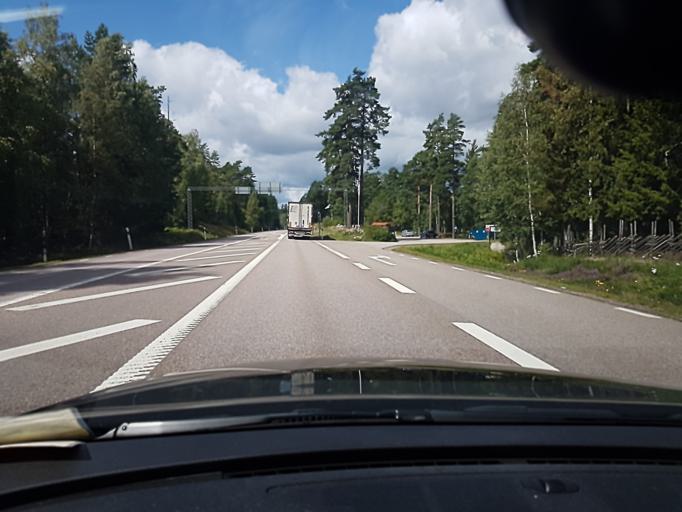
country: SE
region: Kronoberg
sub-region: Lessebo Kommun
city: Lessebo
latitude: 56.7814
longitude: 15.2325
